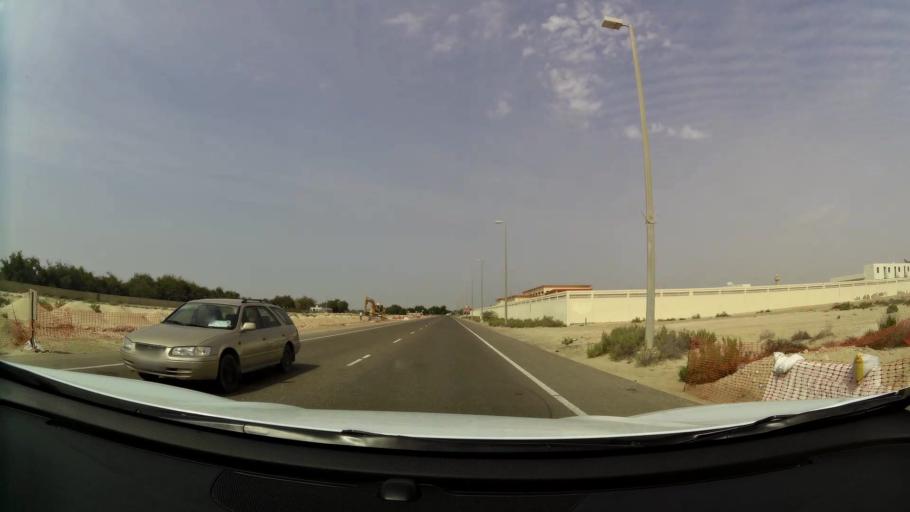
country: AE
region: Abu Dhabi
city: Abu Dhabi
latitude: 24.5623
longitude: 54.6787
